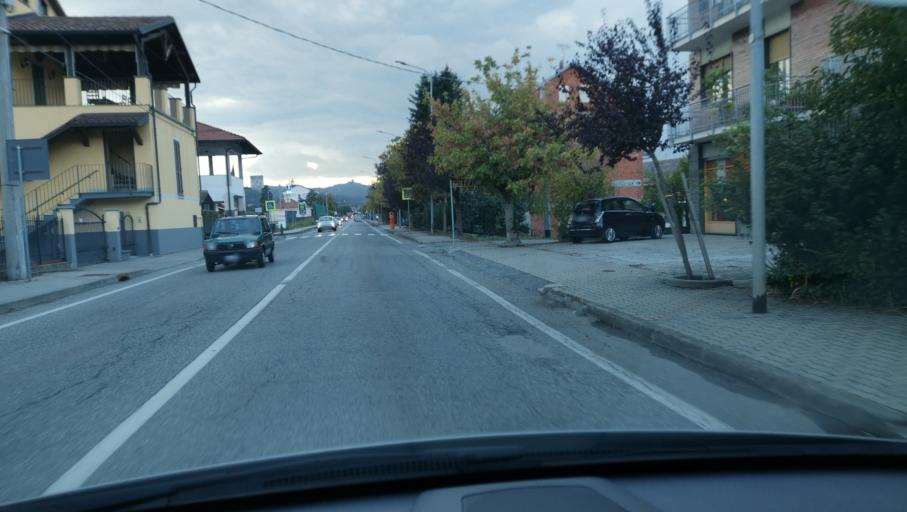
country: IT
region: Piedmont
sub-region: Provincia di Torino
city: San Raffaele Cimena
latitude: 45.1475
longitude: 7.8456
